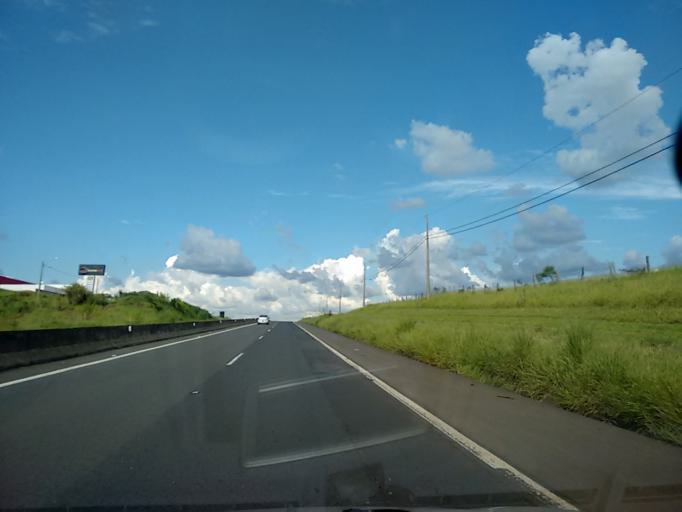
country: BR
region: Sao Paulo
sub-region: Marilia
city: Marilia
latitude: -22.2255
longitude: -49.8931
